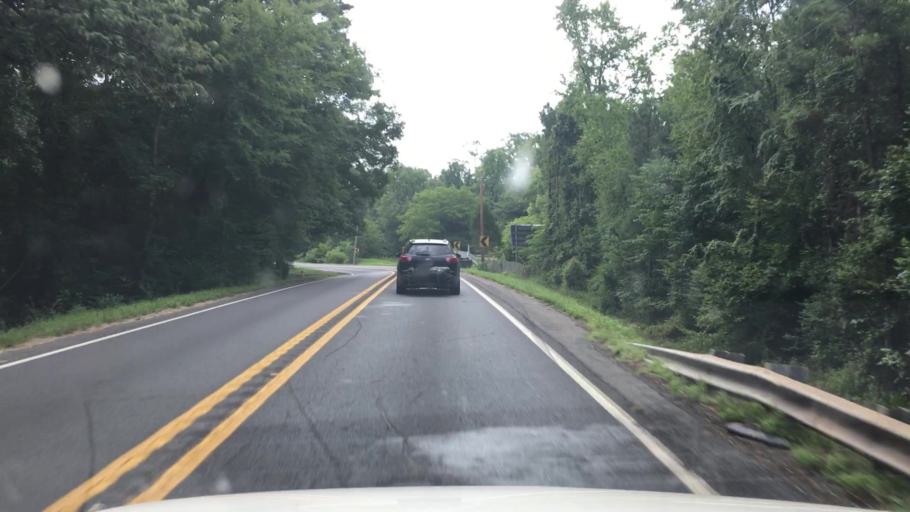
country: US
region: Arkansas
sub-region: Garland County
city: Lake Hamilton
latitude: 34.3408
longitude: -93.1835
